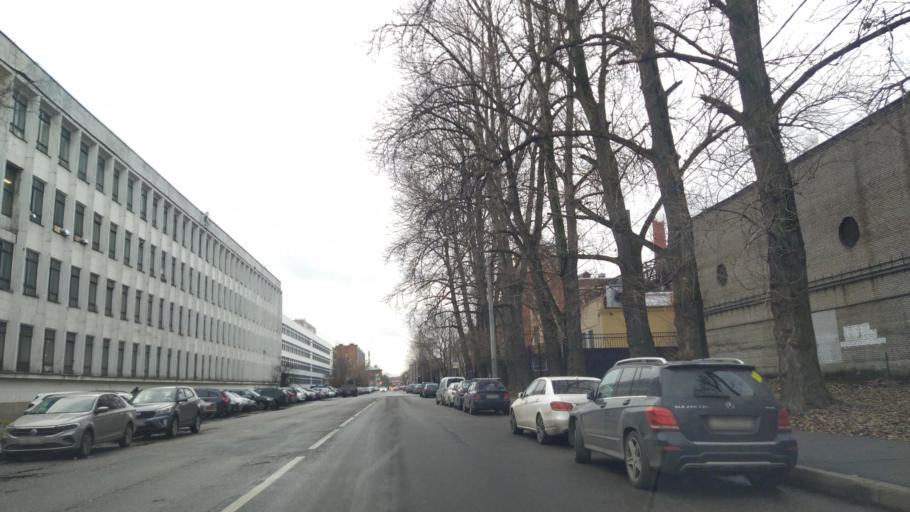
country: RU
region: St.-Petersburg
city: Centralniy
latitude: 59.9178
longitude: 30.3805
